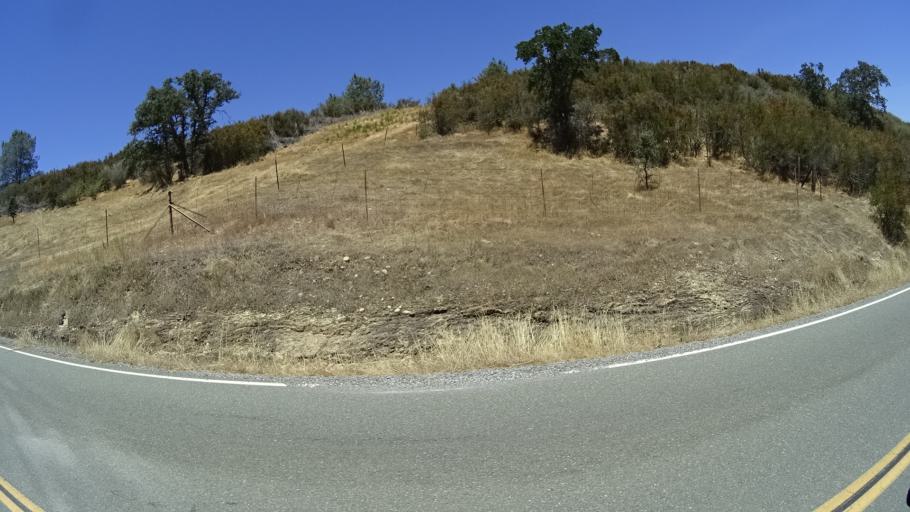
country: US
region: California
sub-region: Calaveras County
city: Valley Springs
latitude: 38.2001
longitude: -120.8900
